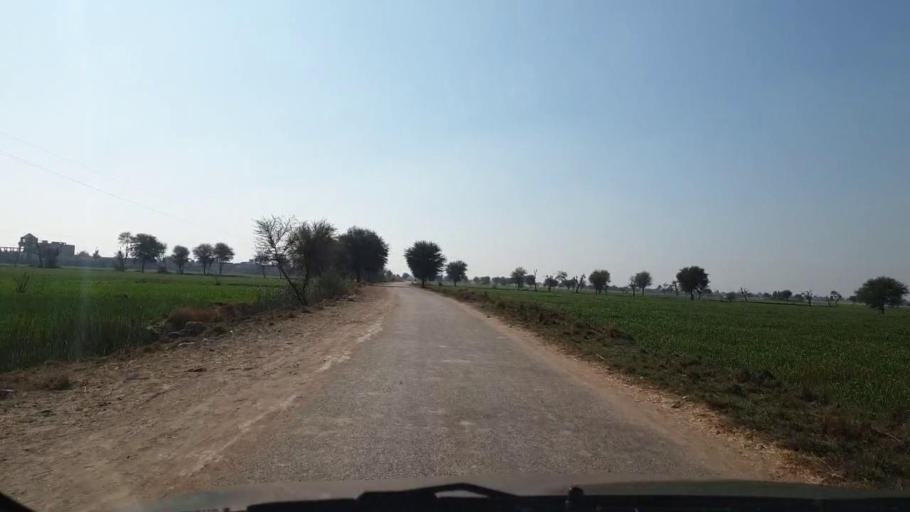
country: PK
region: Sindh
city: Sinjhoro
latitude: 25.9613
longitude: 68.7456
